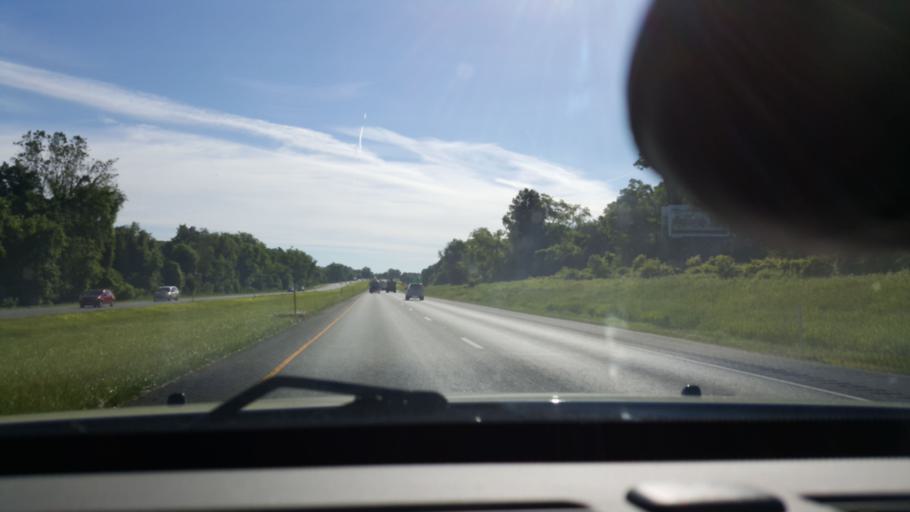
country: US
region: Pennsylvania
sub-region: York County
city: Hallam
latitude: 40.0030
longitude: -76.6264
